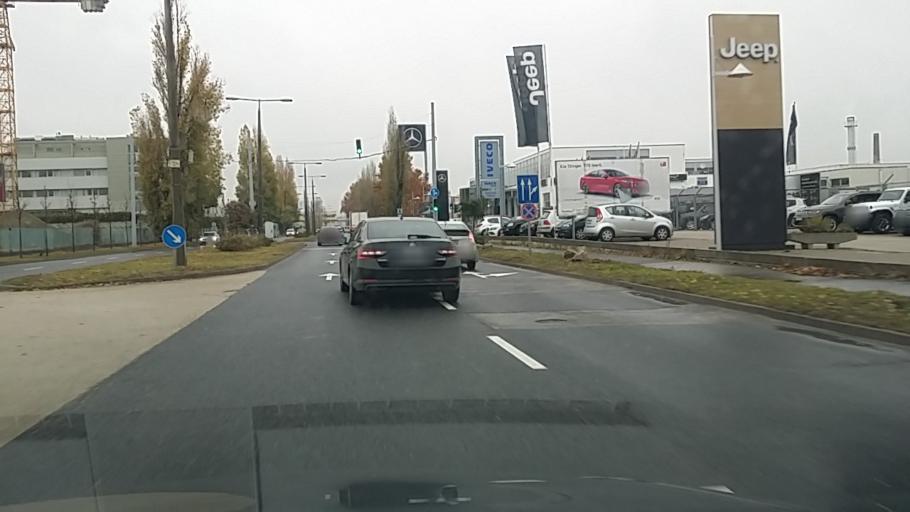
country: HU
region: Budapest
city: Budapest XXII. keruelet
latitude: 47.4436
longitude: 19.0456
